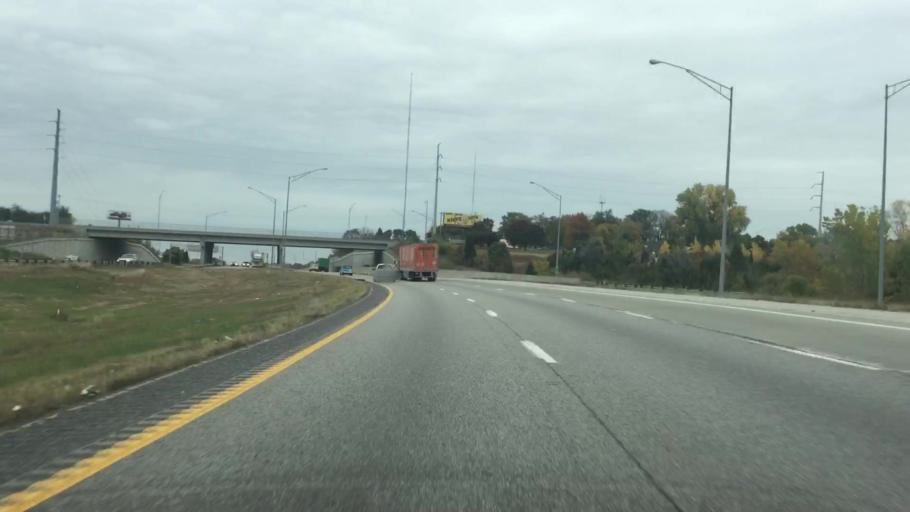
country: US
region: Missouri
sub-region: Jackson County
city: Raytown
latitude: 39.0606
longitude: -94.4884
